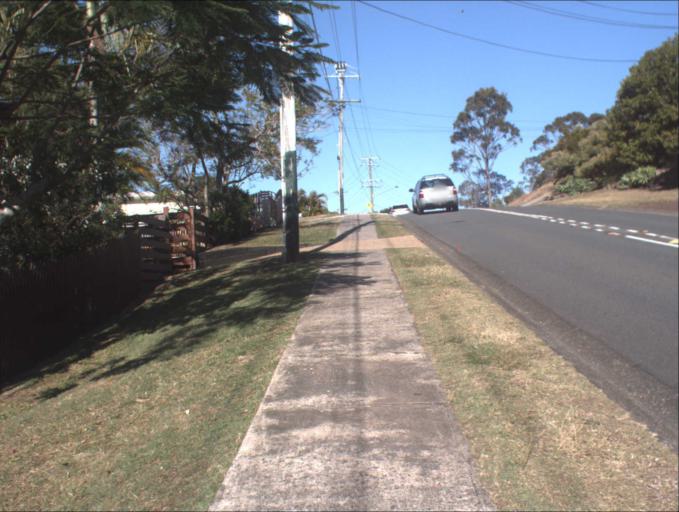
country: AU
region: Queensland
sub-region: Logan
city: Slacks Creek
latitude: -27.6292
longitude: 153.1529
